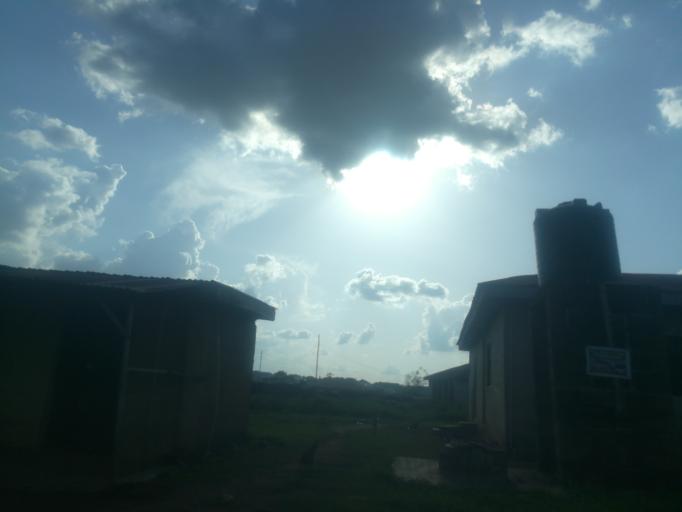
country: NG
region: Oyo
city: Lalupon
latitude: 7.4391
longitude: 3.9817
